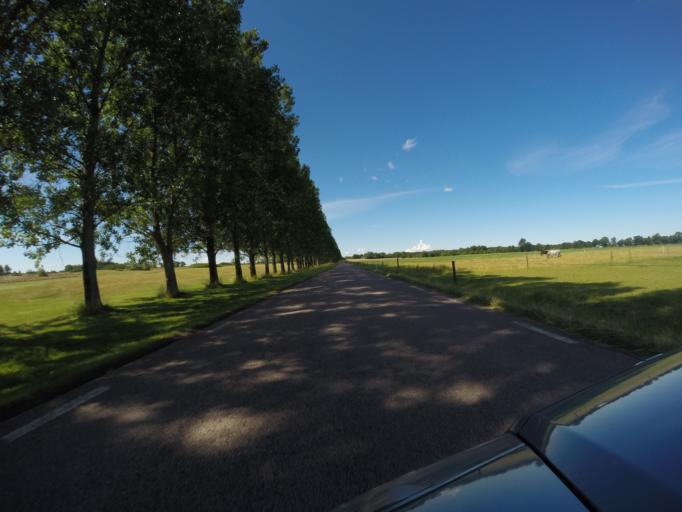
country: SE
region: Skane
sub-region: Helsingborg
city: Odakra
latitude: 56.1315
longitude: 12.7110
